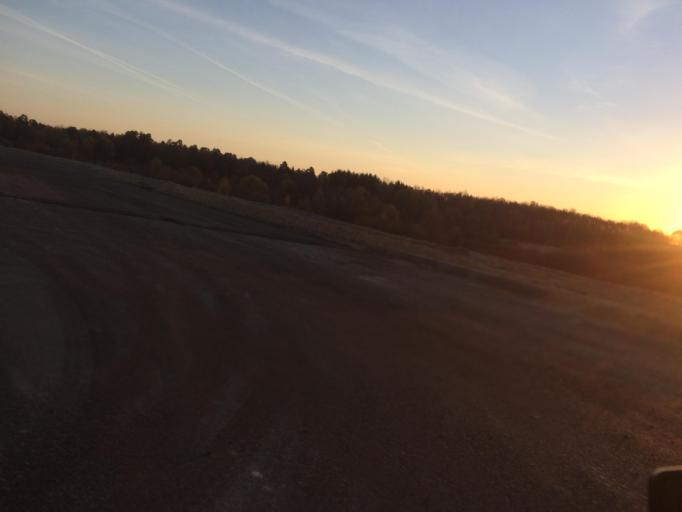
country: RU
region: Mariy-El
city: Yoshkar-Ola
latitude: 56.6179
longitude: 47.9185
